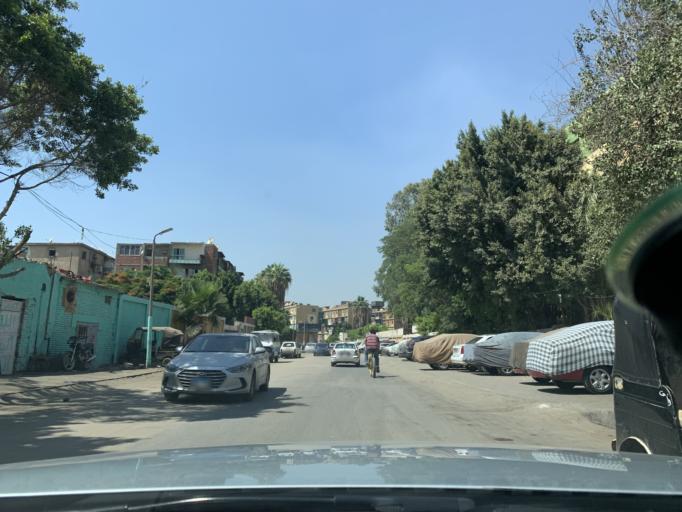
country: EG
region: Muhafazat al Qahirah
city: Cairo
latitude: 30.0742
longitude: 31.2572
